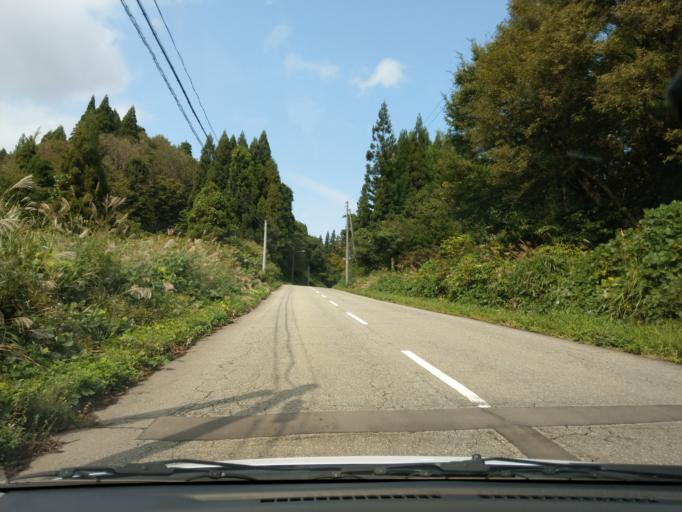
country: JP
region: Akita
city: Omagari
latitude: 39.5107
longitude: 140.3087
